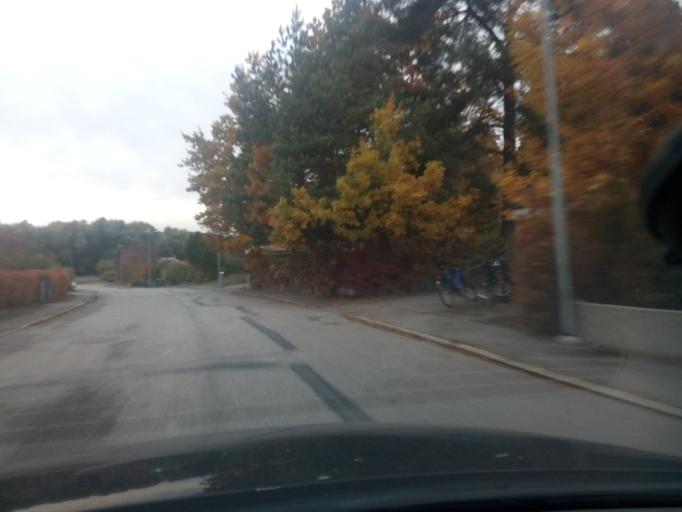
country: SE
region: Soedermanland
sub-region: Nykopings Kommun
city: Nykoping
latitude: 58.7518
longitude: 17.0403
